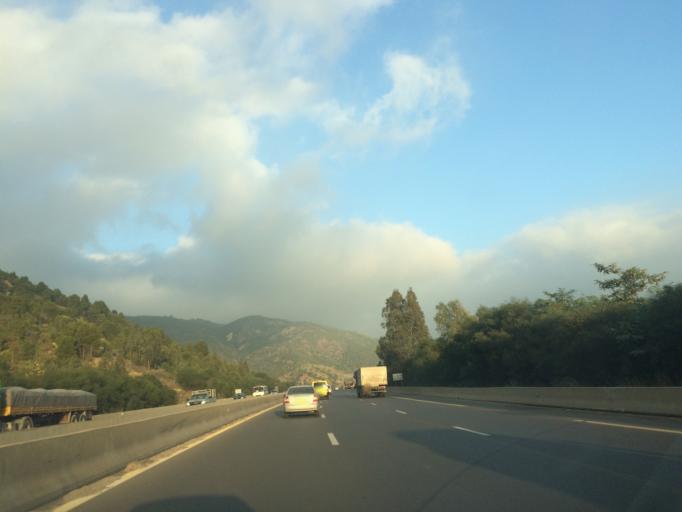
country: DZ
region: Tipaza
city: Hadjout
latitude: 36.3881
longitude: 2.4952
